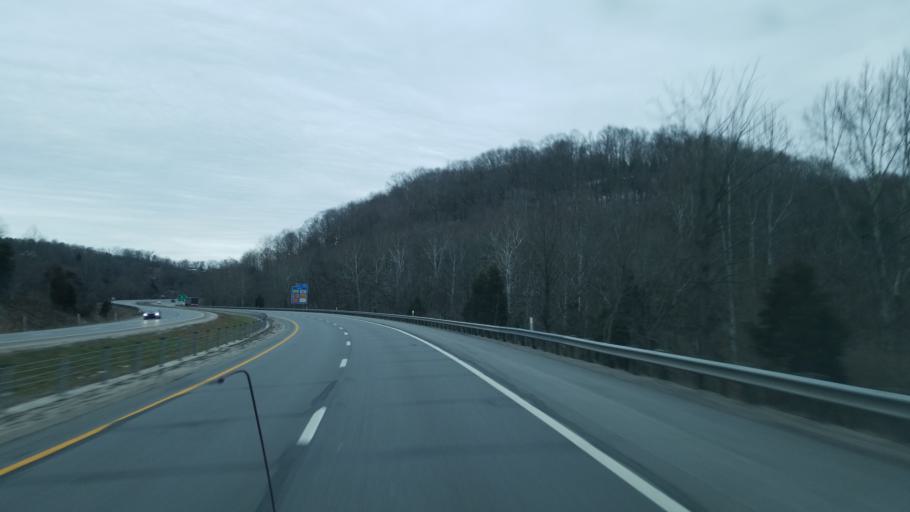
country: US
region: West Virginia
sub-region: Jackson County
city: Ripley
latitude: 38.7675
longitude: -81.7175
